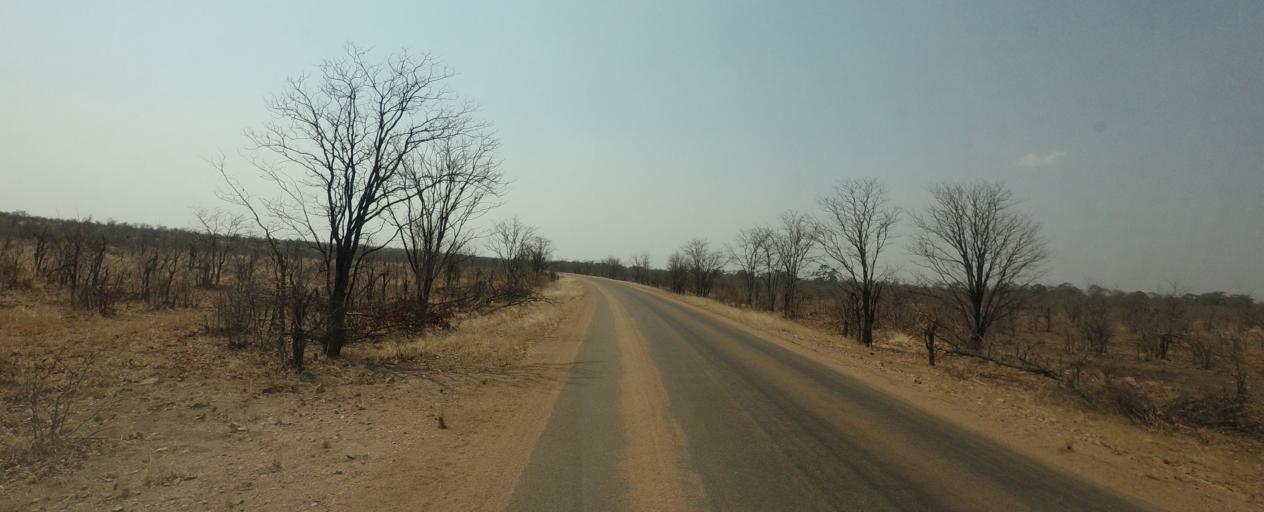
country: ZA
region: Limpopo
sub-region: Mopani District Municipality
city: Giyani
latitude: -23.2132
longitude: 31.3159
